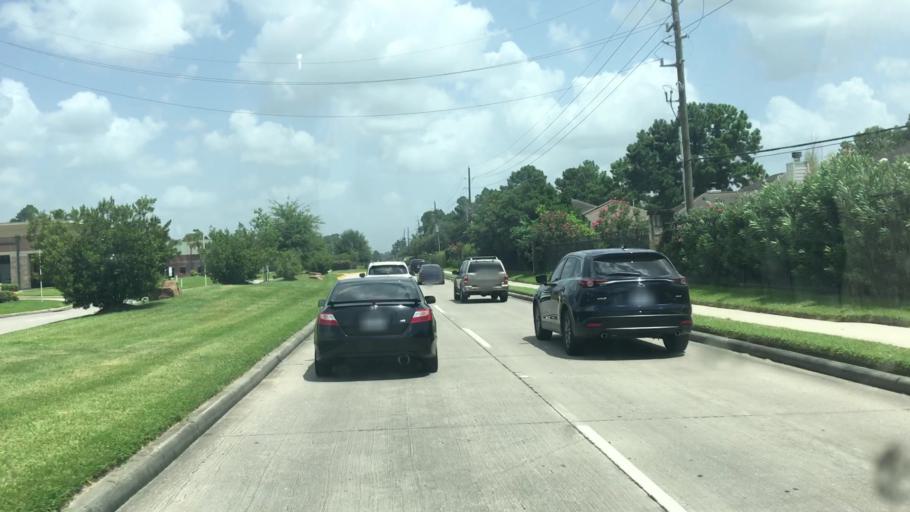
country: US
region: Texas
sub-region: Harris County
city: Atascocita
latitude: 29.9854
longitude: -95.1614
